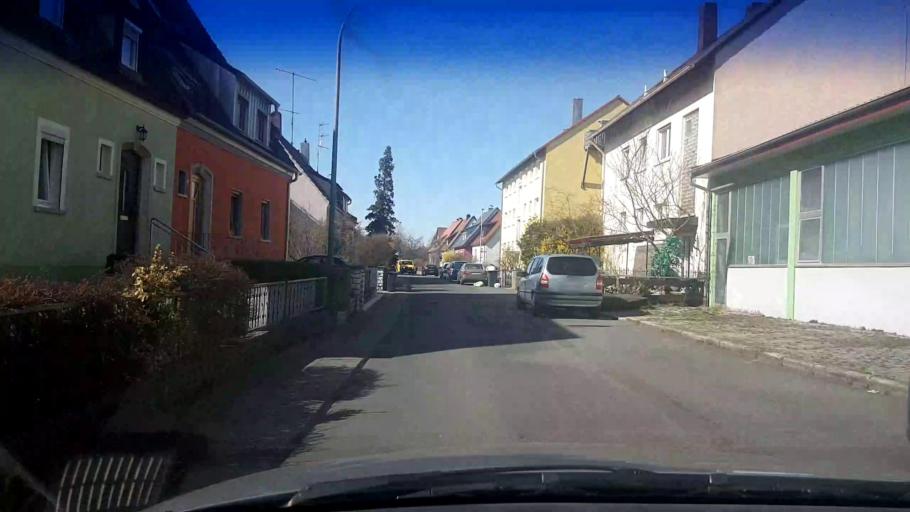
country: DE
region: Bavaria
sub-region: Upper Franconia
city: Kemmern
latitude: 49.9547
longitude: 10.8788
